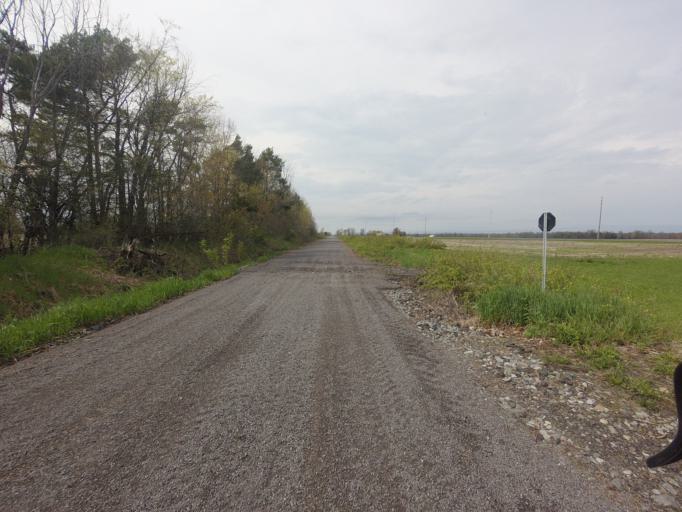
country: CA
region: Ontario
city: Carleton Place
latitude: 45.1805
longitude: -76.1565
